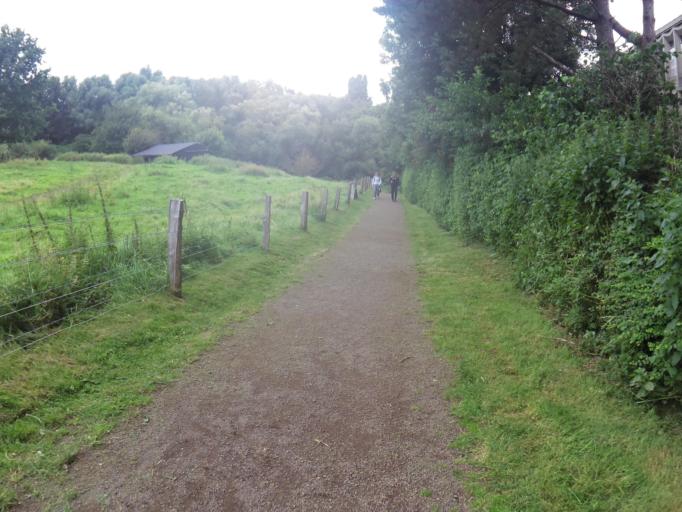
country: BE
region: Flanders
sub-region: Provincie Vlaams-Brabant
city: Dilbeek
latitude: 50.8513
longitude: 4.2956
